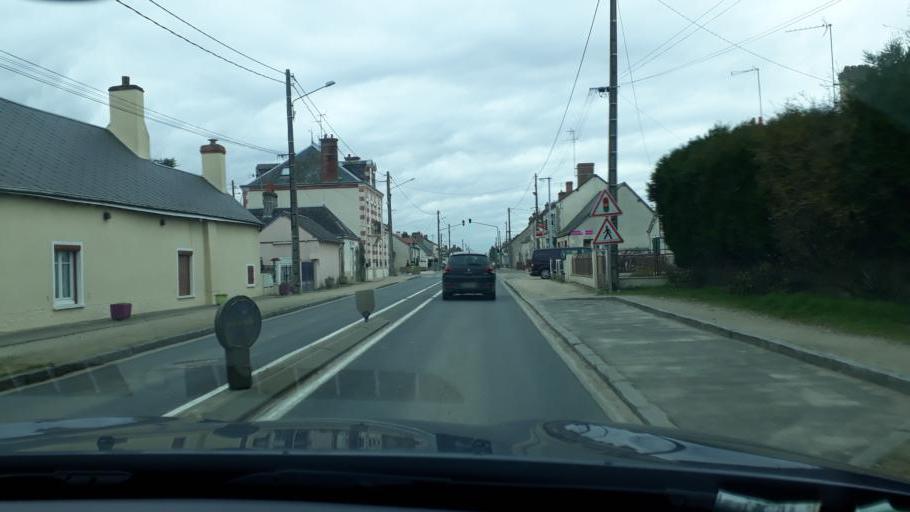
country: FR
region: Centre
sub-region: Departement du Loiret
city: Ascheres-le-Marche
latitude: 48.0418
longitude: 1.9834
